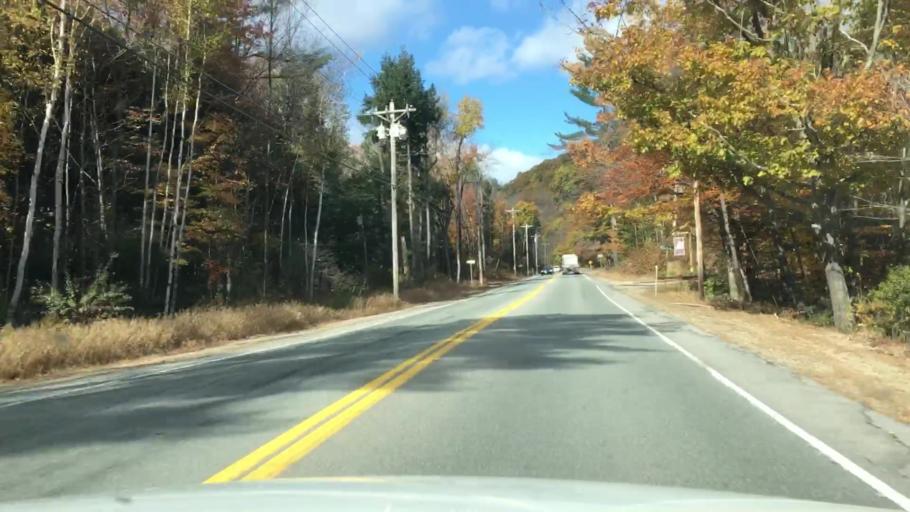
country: US
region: New Hampshire
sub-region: Carroll County
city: North Conway
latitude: 44.1927
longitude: -71.2302
